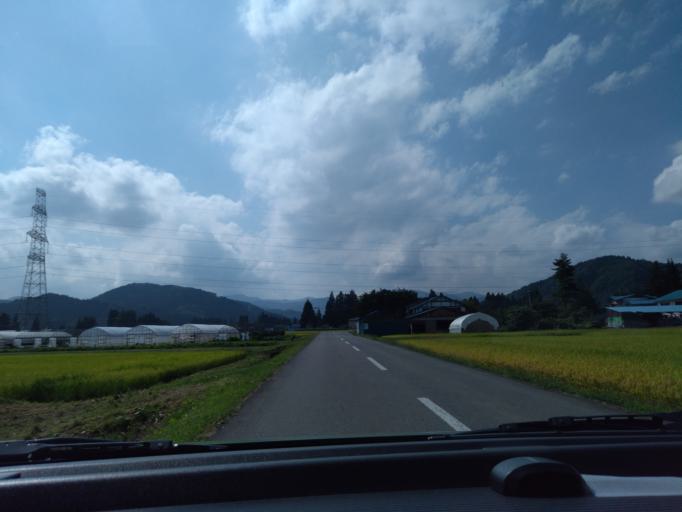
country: JP
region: Iwate
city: Shizukuishi
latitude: 39.6850
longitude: 140.9318
